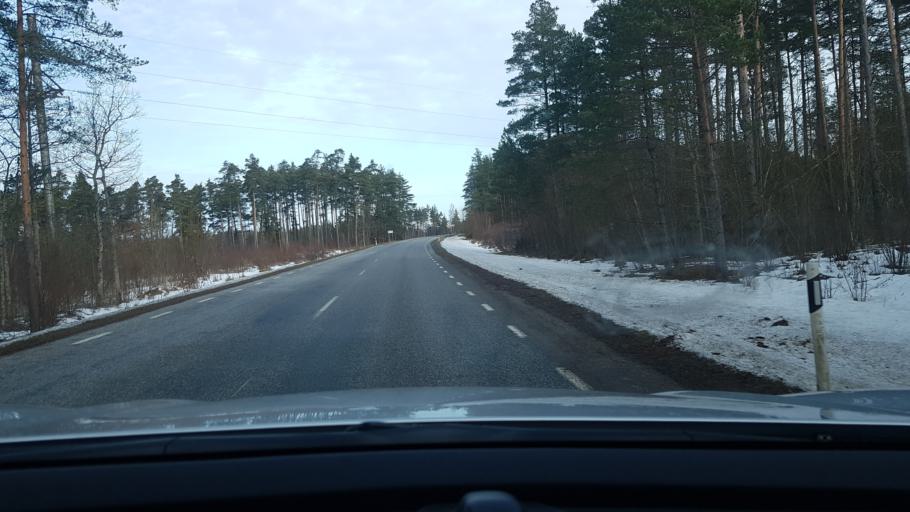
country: EE
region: Saare
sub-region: Kuressaare linn
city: Kuressaare
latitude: 58.4396
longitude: 22.7048
